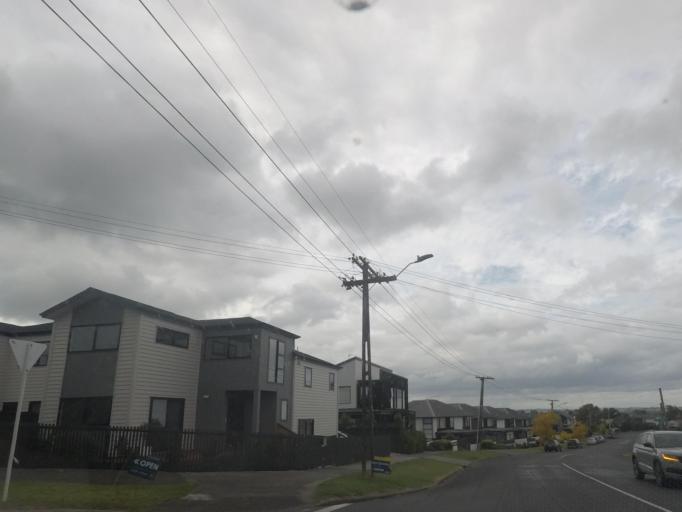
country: NZ
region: Auckland
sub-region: Auckland
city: Tamaki
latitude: -36.8703
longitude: 174.8746
